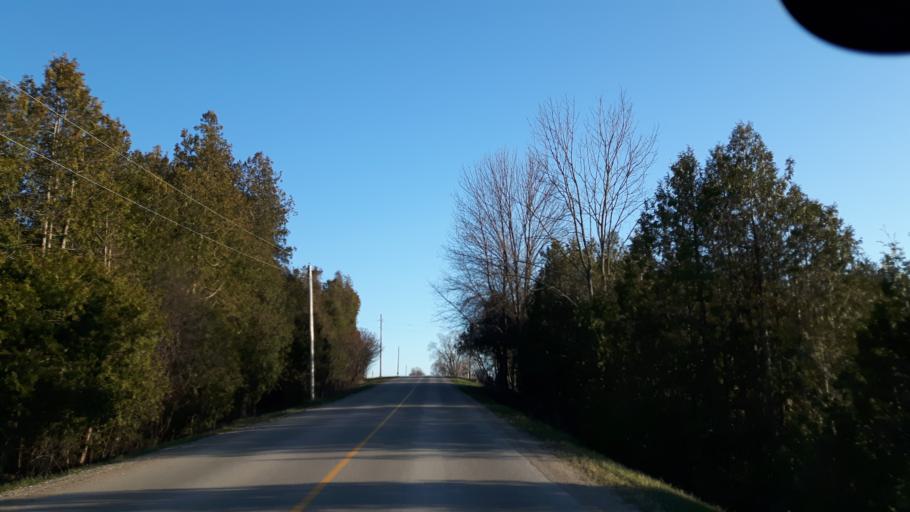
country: CA
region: Ontario
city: Goderich
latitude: 43.6678
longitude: -81.6847
